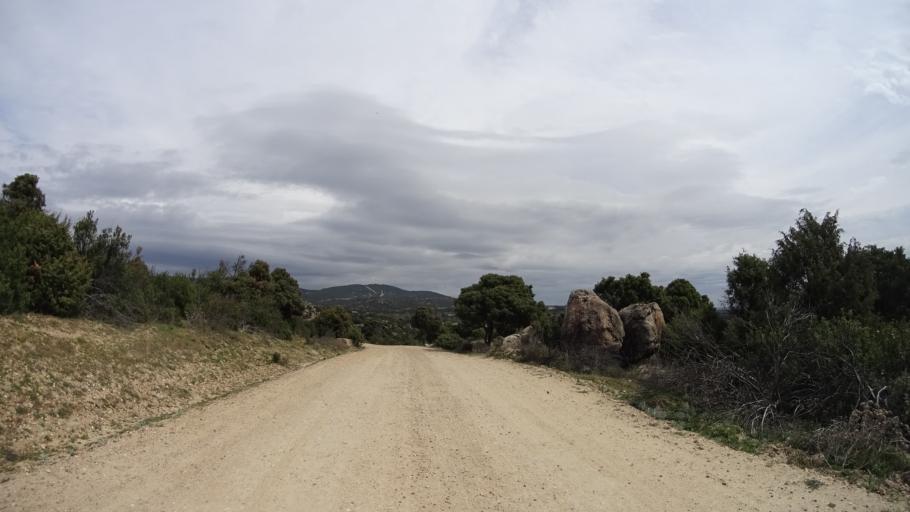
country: ES
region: Madrid
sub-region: Provincia de Madrid
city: Hoyo de Manzanares
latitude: 40.6171
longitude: -3.8771
